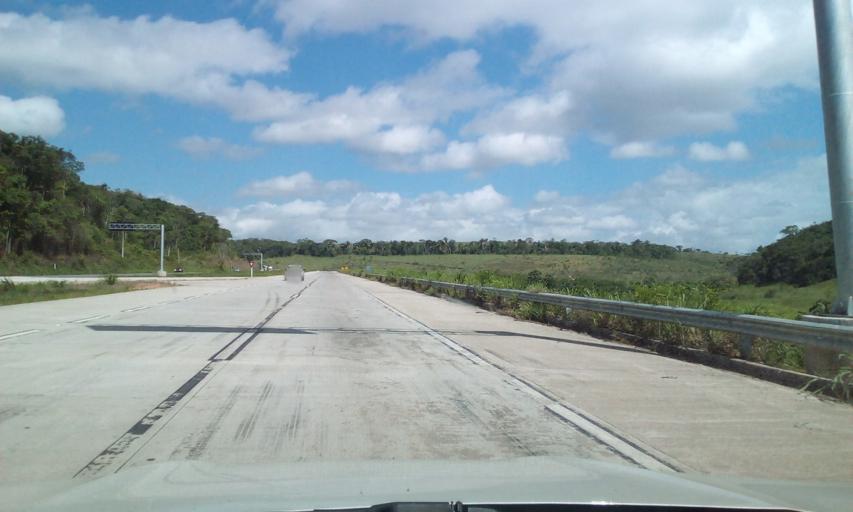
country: BR
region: Alagoas
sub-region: Rio Largo
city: Rio Largo
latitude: -9.5032
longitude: -35.9142
